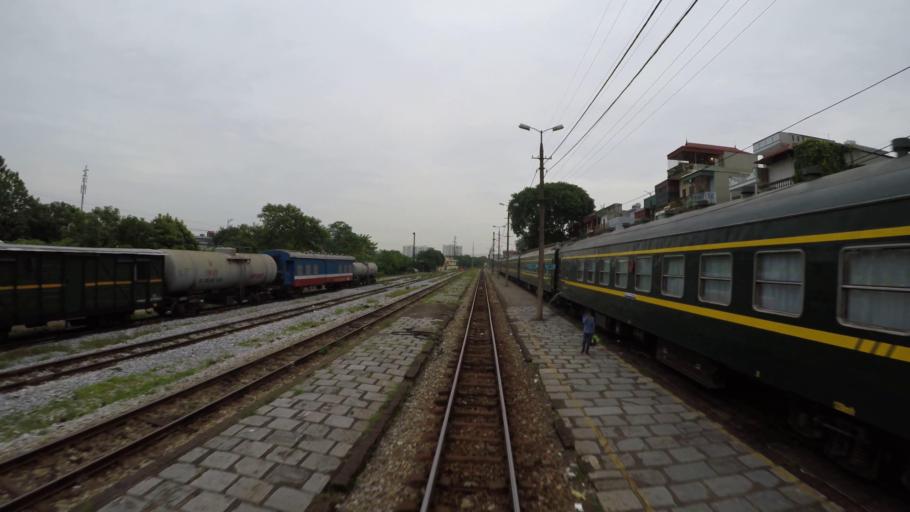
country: VN
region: Ha Noi
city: Trau Quy
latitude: 21.0320
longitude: 105.9091
